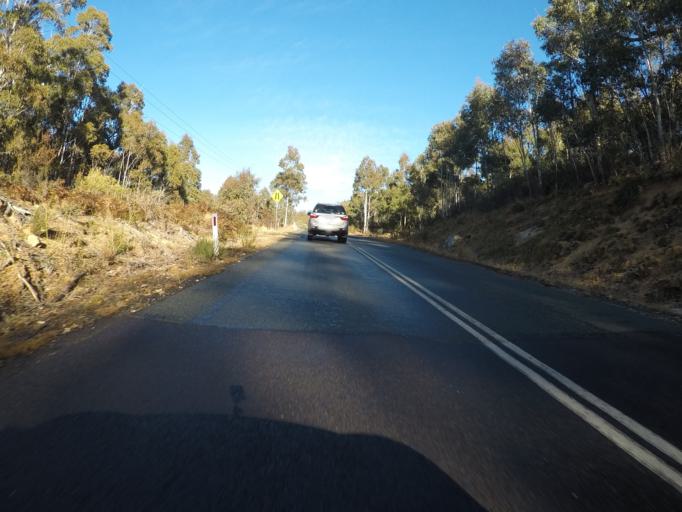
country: AU
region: Australian Capital Territory
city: Macarthur
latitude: -35.4927
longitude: 148.9255
